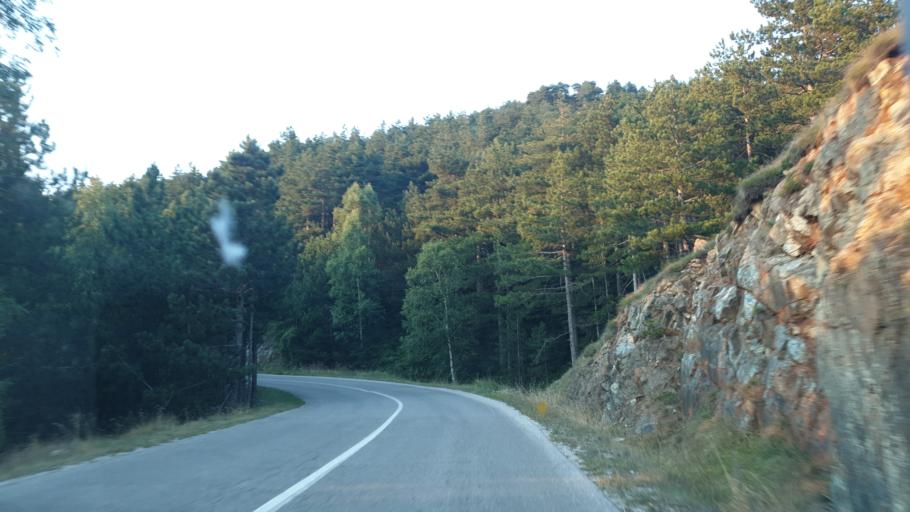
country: RS
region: Central Serbia
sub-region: Zlatiborski Okrug
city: Kosjeric
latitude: 44.0903
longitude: 19.9929
